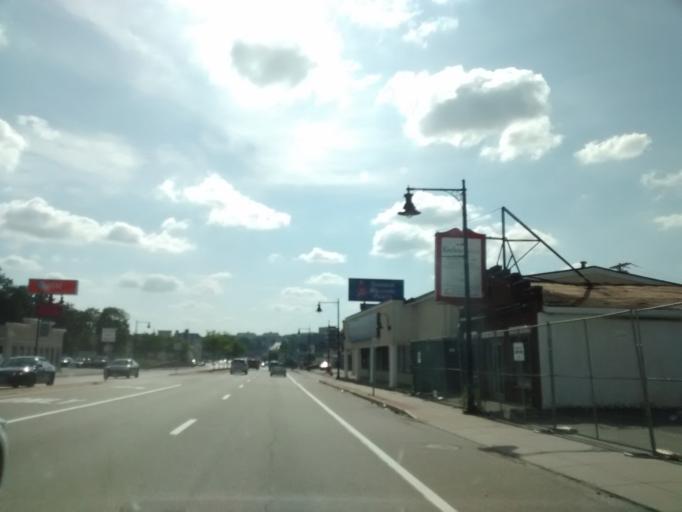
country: US
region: Massachusetts
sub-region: Worcester County
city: Hamilton
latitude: 42.2751
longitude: -71.7467
